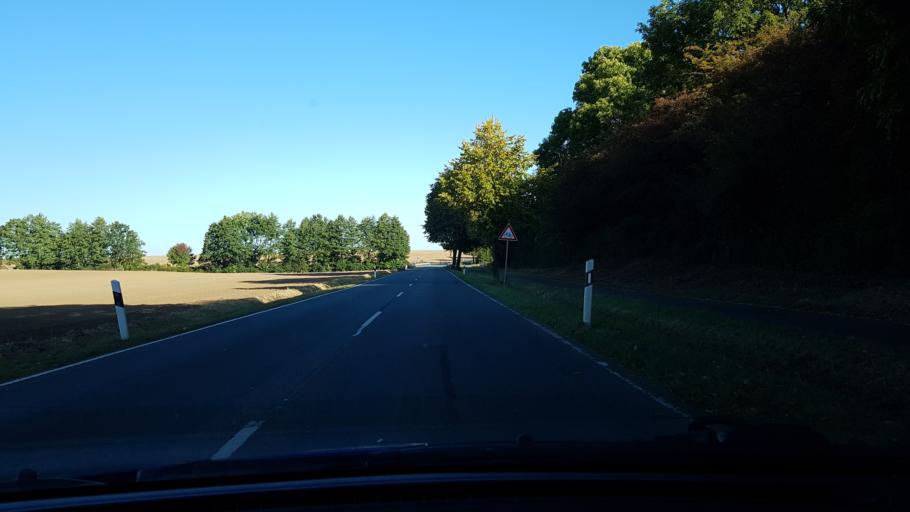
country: DE
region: Lower Saxony
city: Hulsede
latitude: 52.2316
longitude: 9.3758
